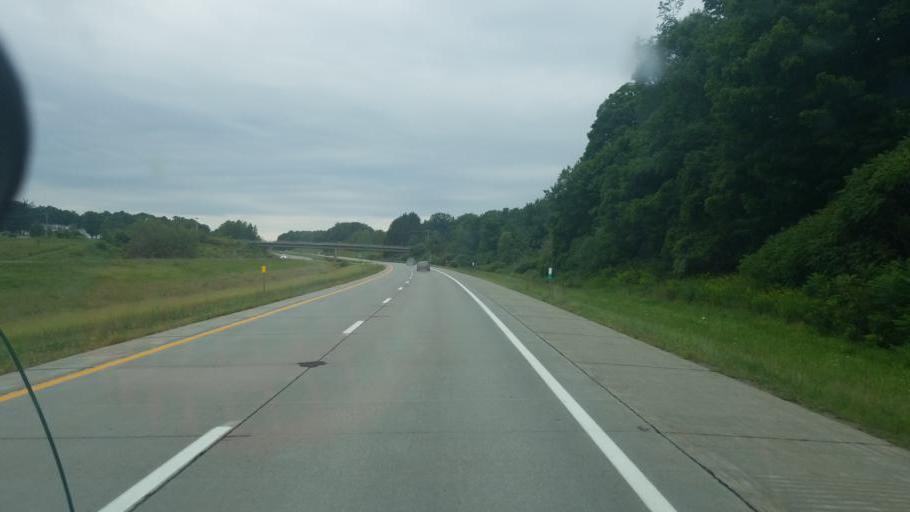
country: US
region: New York
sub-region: Chautauqua County
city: Lakewood
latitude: 42.1533
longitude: -79.4211
